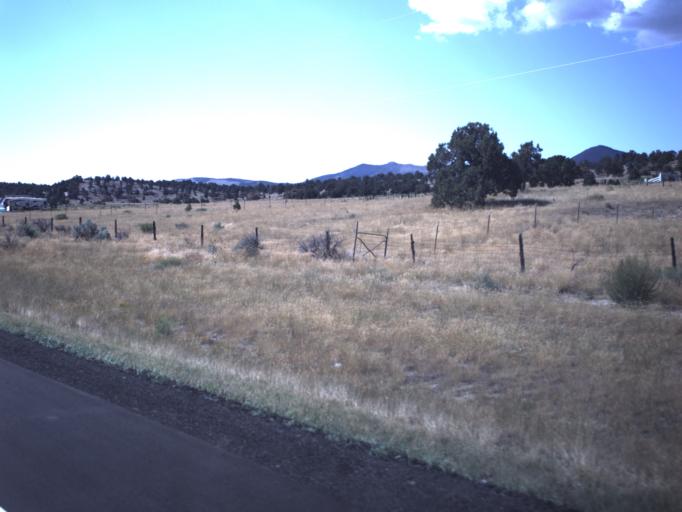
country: US
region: Utah
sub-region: Utah County
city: Eagle Mountain
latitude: 40.0256
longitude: -112.2819
